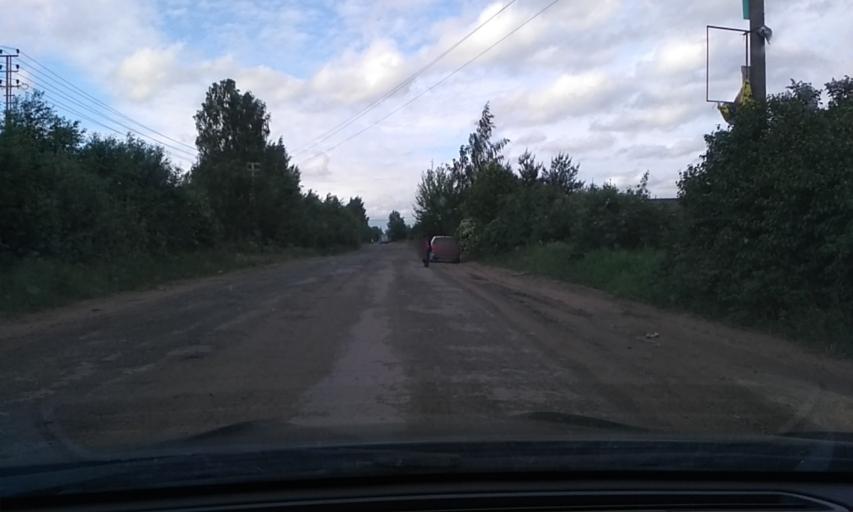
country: RU
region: Leningrad
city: Otradnoye
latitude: 59.7892
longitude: 30.7909
